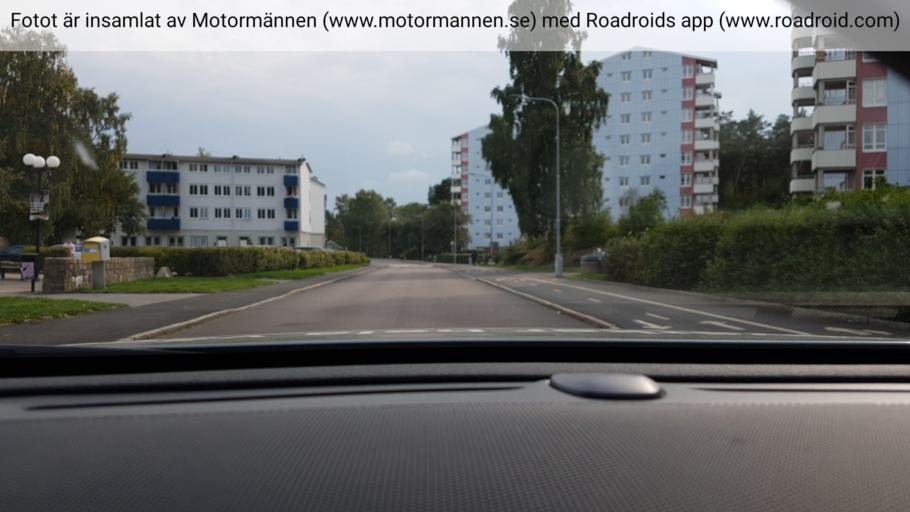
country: SE
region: Vaestra Goetaland
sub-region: Goteborg
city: Majorna
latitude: 57.7178
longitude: 11.8868
